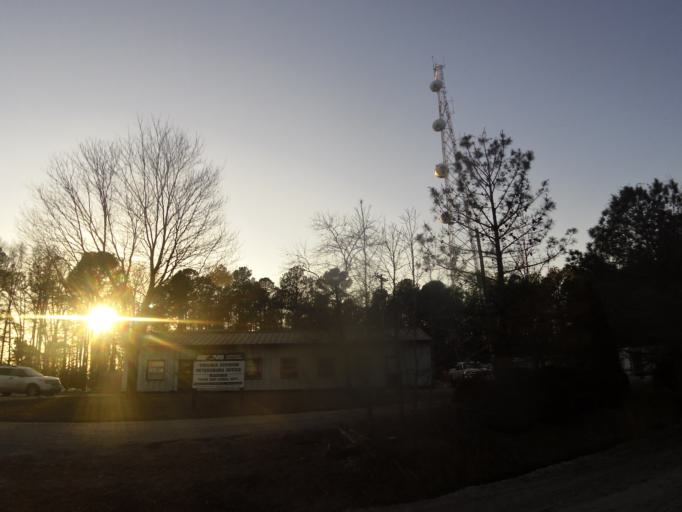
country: US
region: Virginia
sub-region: City of Petersburg
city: Petersburg
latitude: 37.1806
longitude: -77.4218
